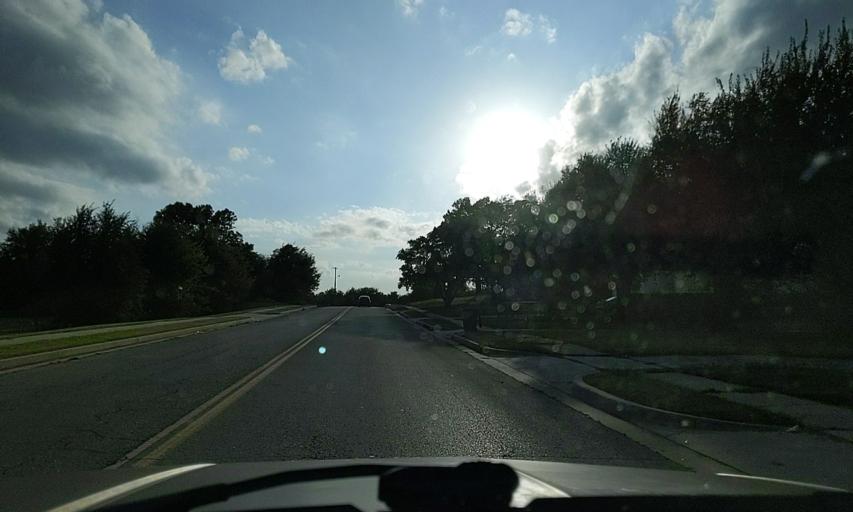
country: US
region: Oklahoma
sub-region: Tulsa County
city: Tulsa
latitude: 36.1943
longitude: -95.9825
